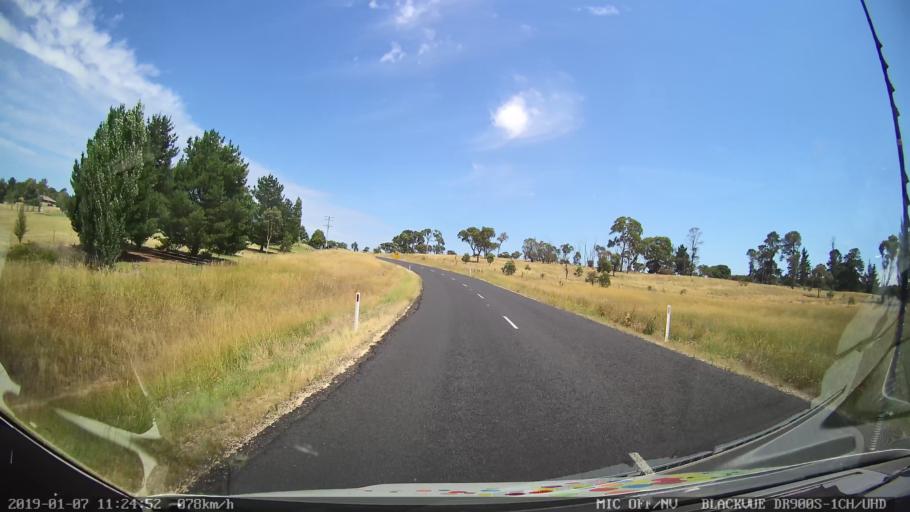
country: AU
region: New South Wales
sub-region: Armidale Dumaresq
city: Armidale
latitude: -30.4622
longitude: 151.6086
